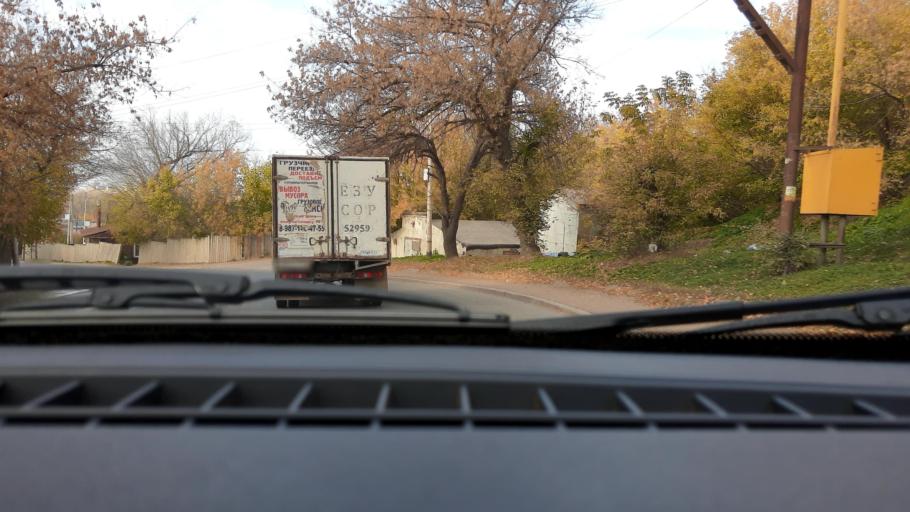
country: RU
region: Bashkortostan
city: Ufa
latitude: 54.7427
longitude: 55.9371
